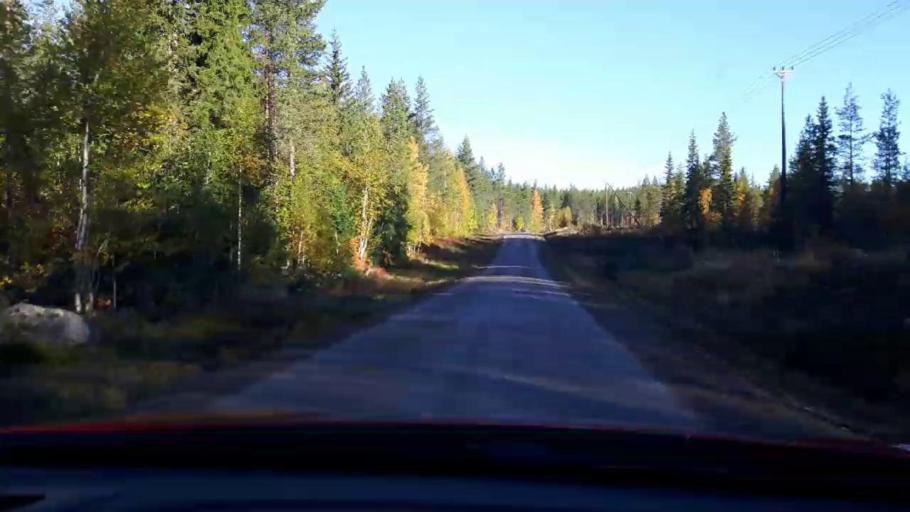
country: SE
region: Jaemtland
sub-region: Stroemsunds Kommun
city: Stroemsund
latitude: 64.3786
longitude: 15.1493
